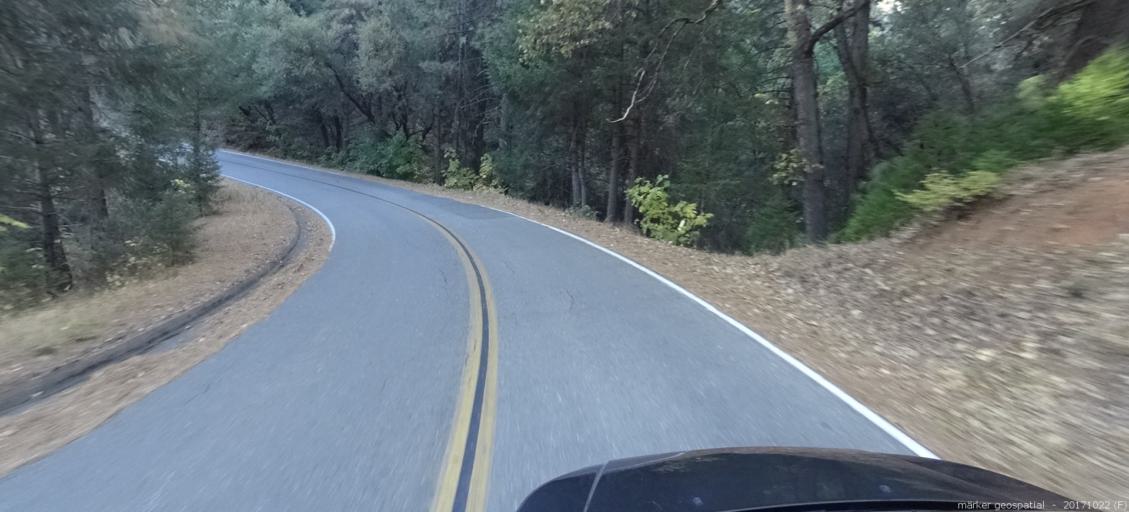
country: US
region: California
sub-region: Shasta County
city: Shasta Lake
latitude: 40.8754
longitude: -122.2463
